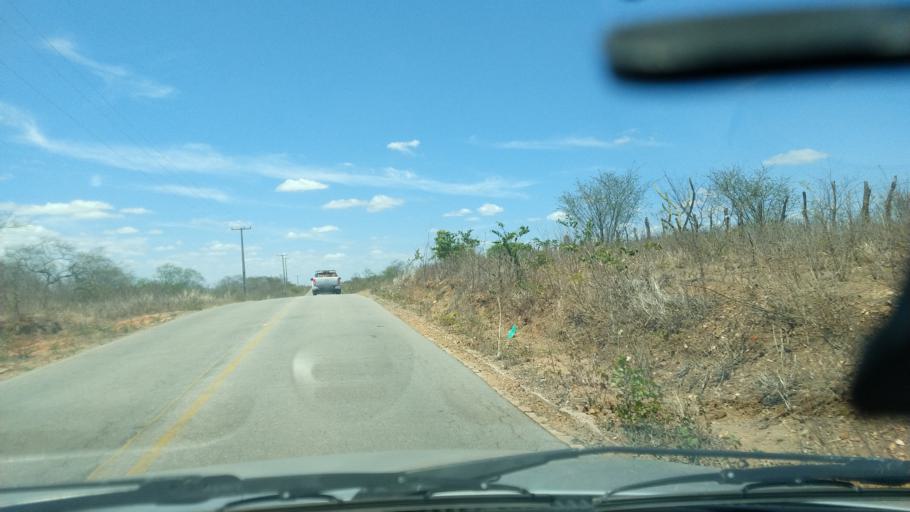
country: BR
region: Rio Grande do Norte
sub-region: Sao Paulo Do Potengi
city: Sao Paulo do Potengi
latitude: -5.9099
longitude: -35.5979
